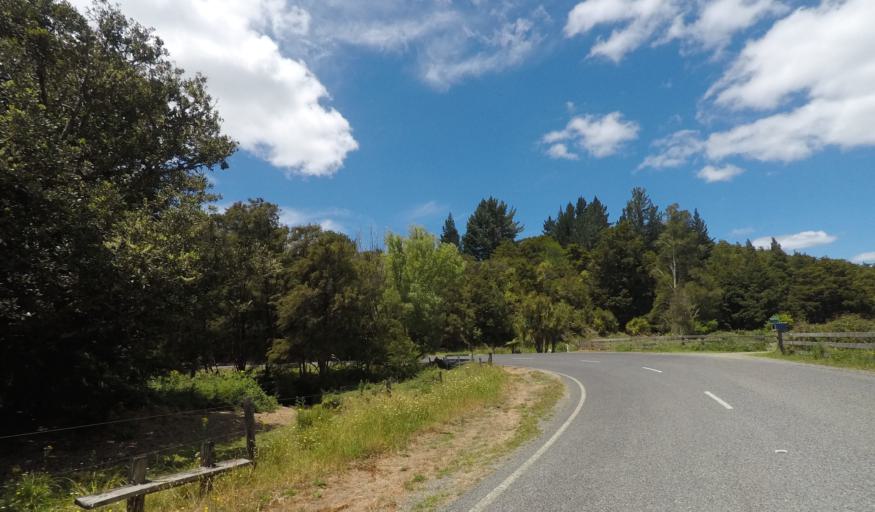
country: NZ
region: Northland
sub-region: Whangarei
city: Ngunguru
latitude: -35.5062
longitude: 174.4053
